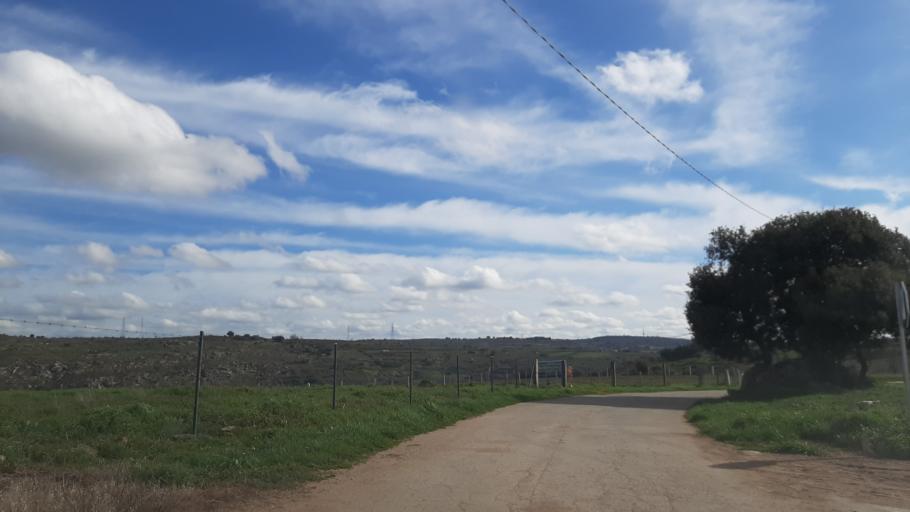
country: ES
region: Castille and Leon
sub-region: Provincia de Salamanca
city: Villarino de los Aires
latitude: 41.2484
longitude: -6.5224
